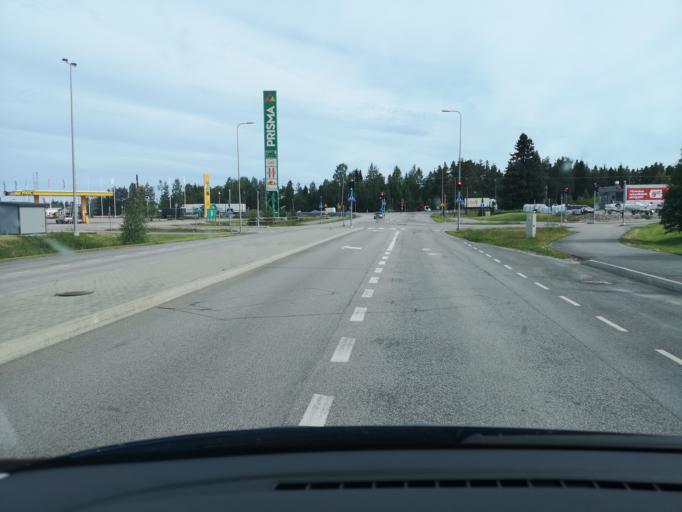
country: FI
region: Northern Ostrobothnia
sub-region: Ylivieska
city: Ylivieska
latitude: 64.0620
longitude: 24.5598
